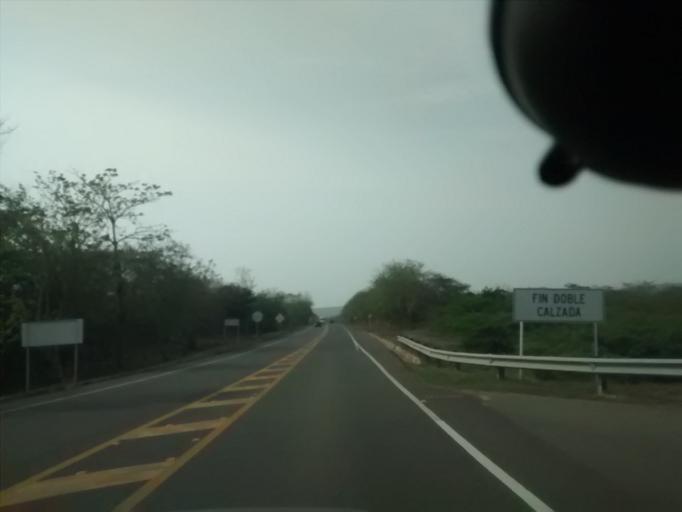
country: CO
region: Bolivar
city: Clemencia
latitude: 10.5804
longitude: -75.4495
